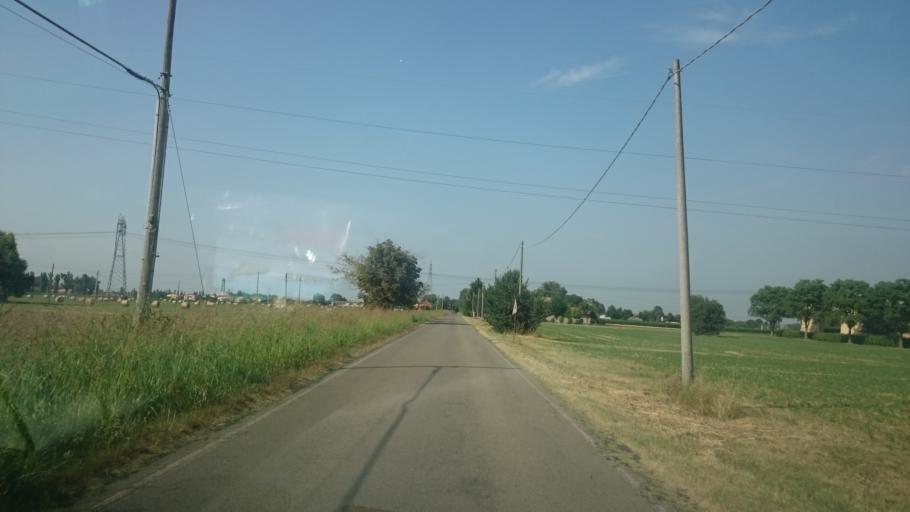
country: IT
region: Emilia-Romagna
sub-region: Provincia di Reggio Emilia
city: Bagno
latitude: 44.6377
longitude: 10.7430
